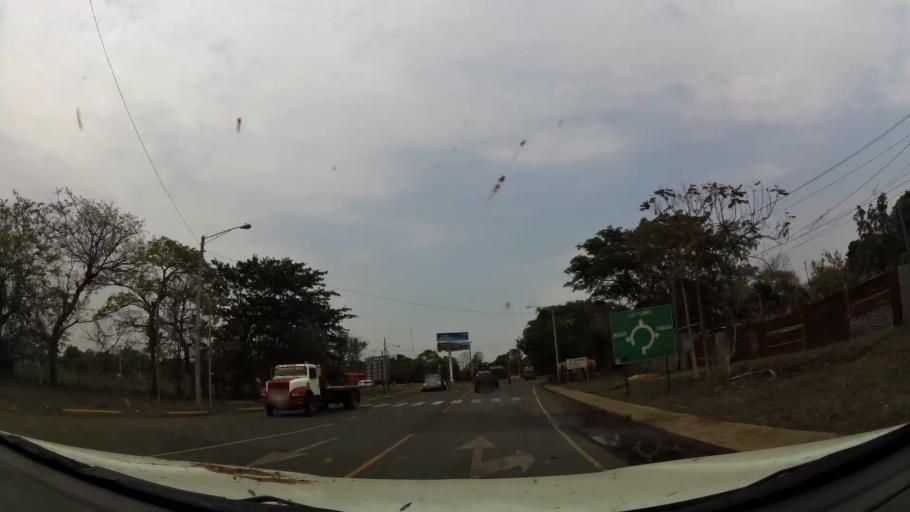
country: NI
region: Masaya
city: Masaya
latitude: 11.9737
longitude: -86.0765
